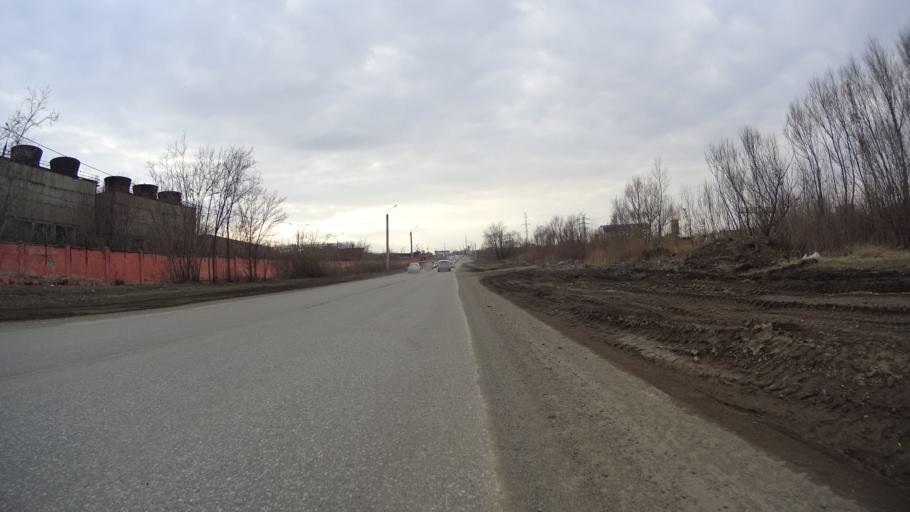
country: RU
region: Chelyabinsk
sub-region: Gorod Chelyabinsk
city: Chelyabinsk
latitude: 55.1571
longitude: 61.4919
